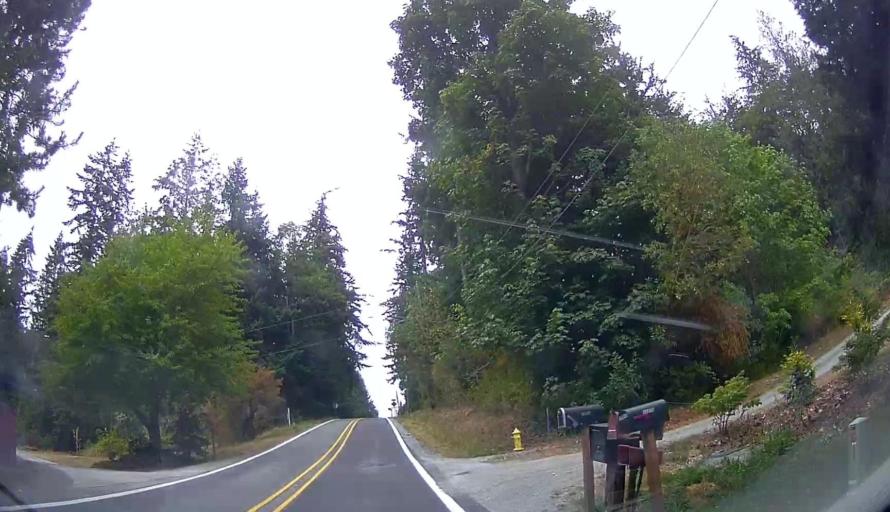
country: US
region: Washington
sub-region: Snohomish County
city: Warm Beach
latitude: 48.1578
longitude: -122.3575
